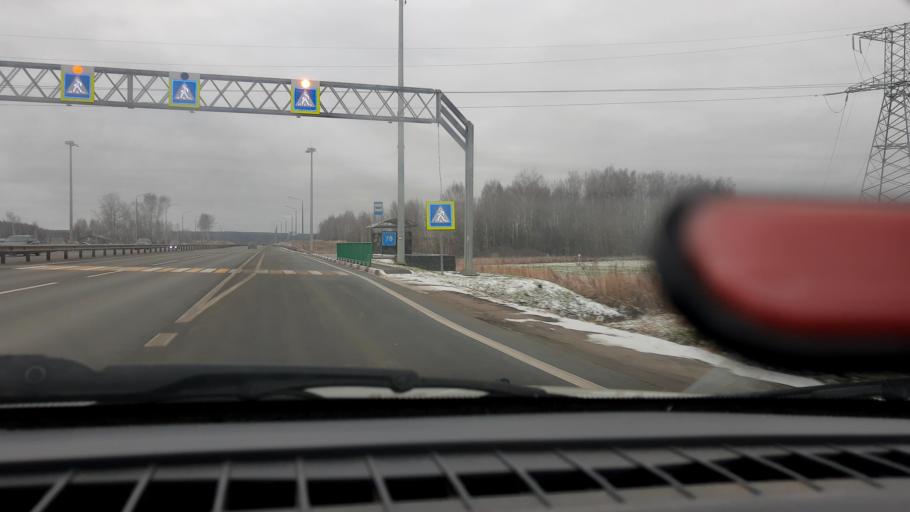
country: RU
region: Nizjnij Novgorod
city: Burevestnik
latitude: 56.1049
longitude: 43.9178
